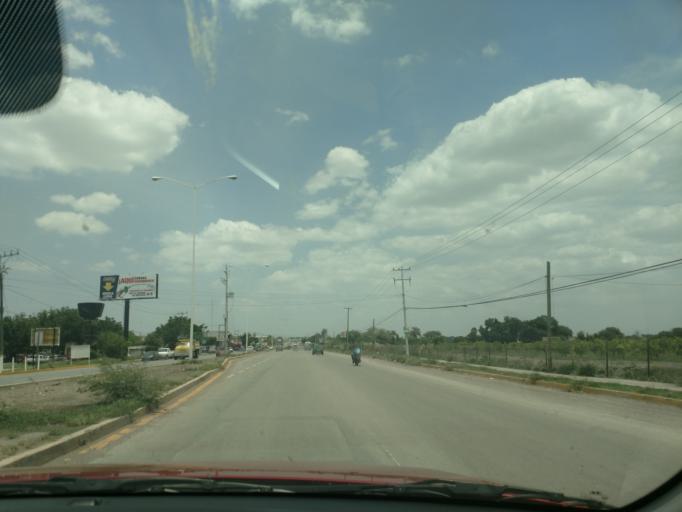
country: MX
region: San Luis Potosi
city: Ciudad Fernandez
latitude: 21.9355
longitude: -100.0264
